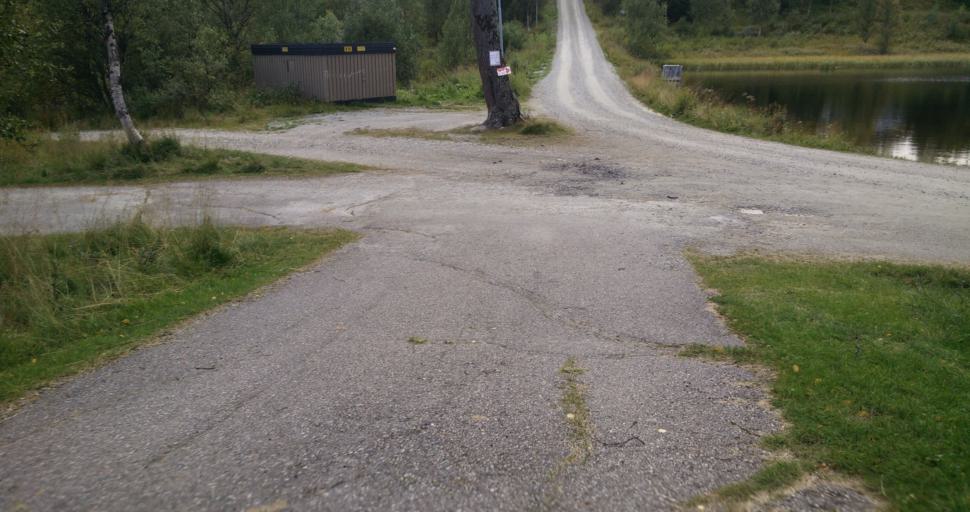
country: NO
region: Sor-Trondelag
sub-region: Tydal
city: Aas
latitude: 62.6393
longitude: 12.4175
